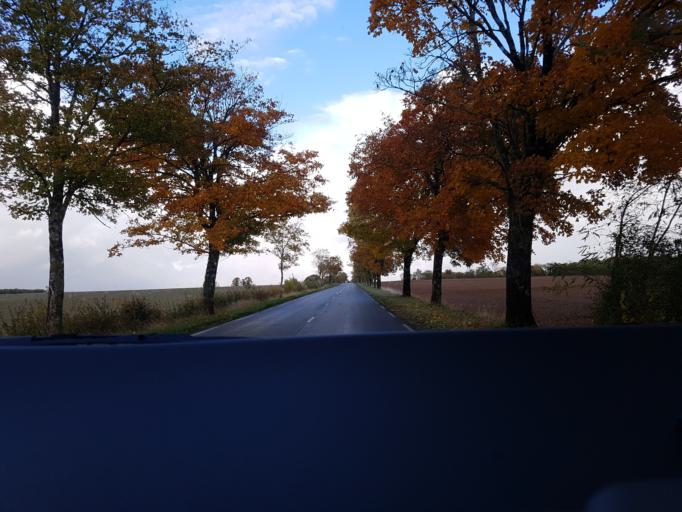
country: FR
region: Poitou-Charentes
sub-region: Departement des Deux-Sevres
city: Brioux-sur-Boutonne
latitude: 46.0934
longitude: -0.2826
